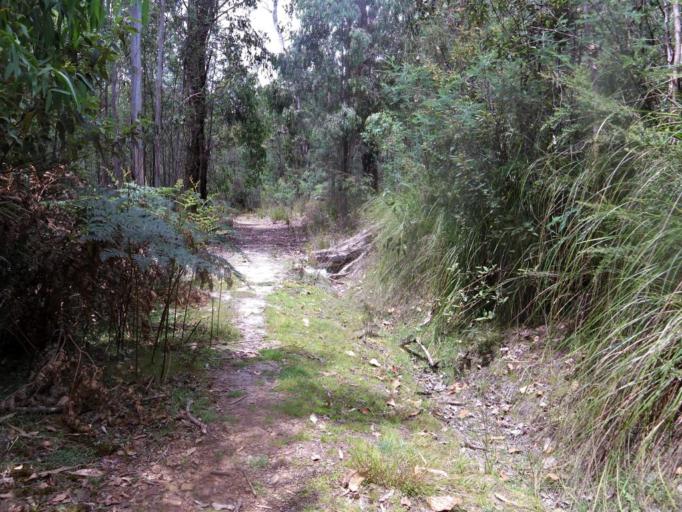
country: AU
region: Victoria
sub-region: Yarra Ranges
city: Healesville
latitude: -37.4370
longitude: 145.5768
